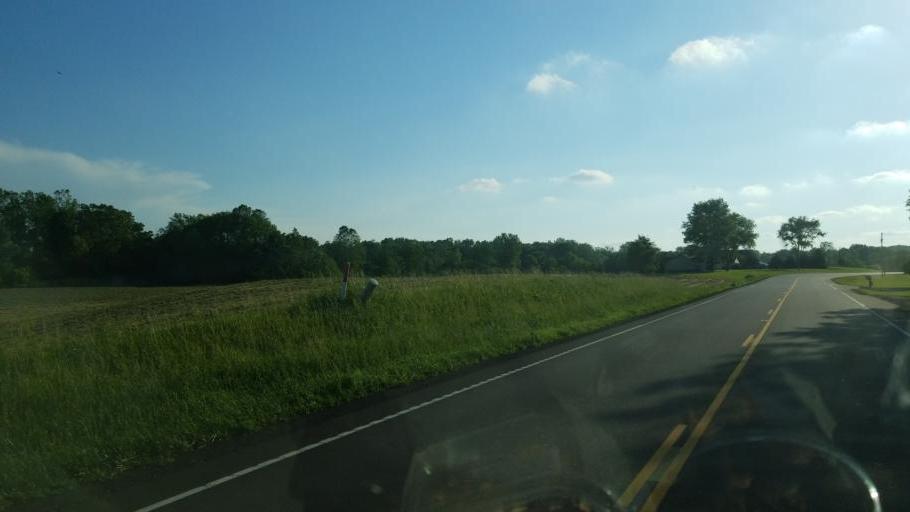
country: US
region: Ohio
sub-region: Knox County
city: Fredericktown
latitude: 40.4626
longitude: -82.6327
